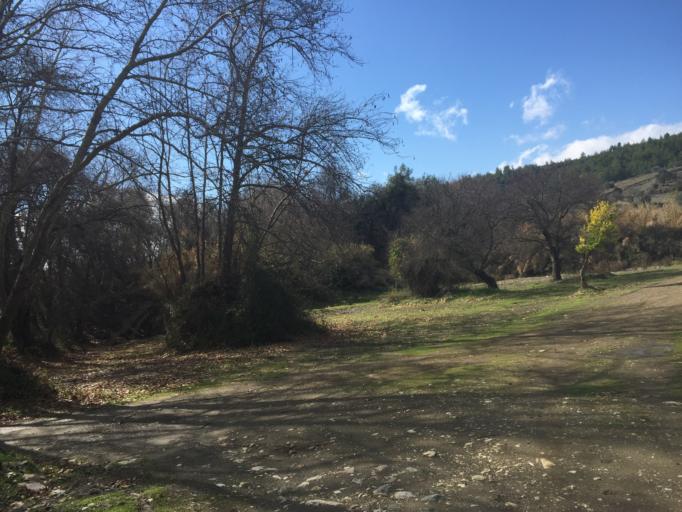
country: CY
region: Limassol
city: Pachna
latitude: 34.8867
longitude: 32.6774
